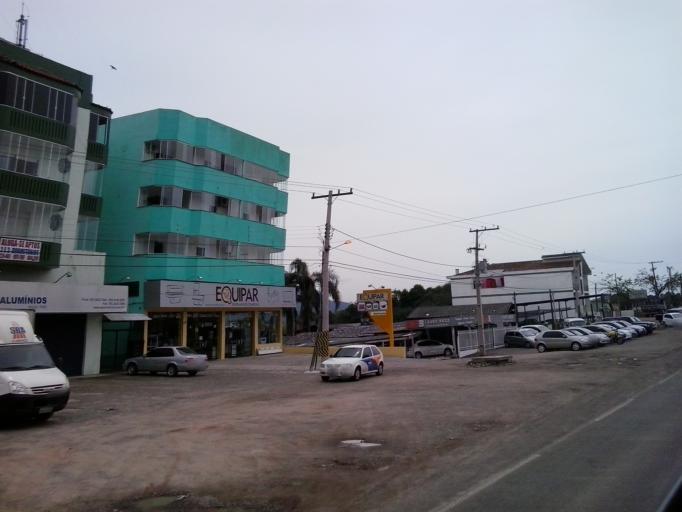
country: BR
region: Rio Grande do Sul
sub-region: Santa Maria
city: Santa Maria
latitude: -29.6960
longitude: -53.7715
